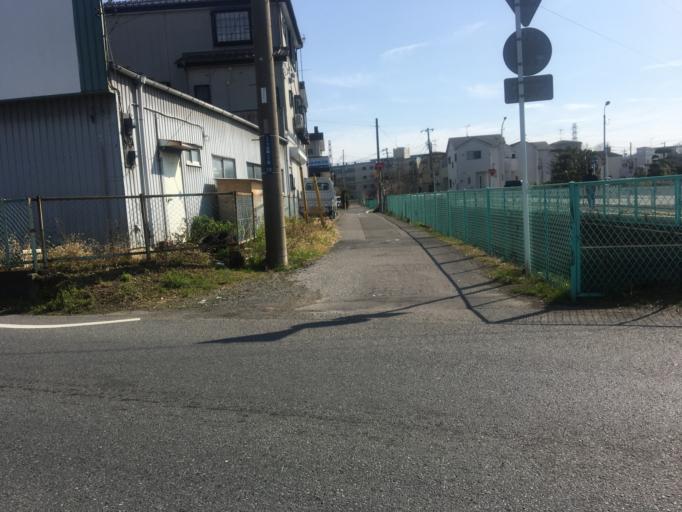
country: JP
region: Saitama
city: Shiki
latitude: 35.8327
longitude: 139.5962
